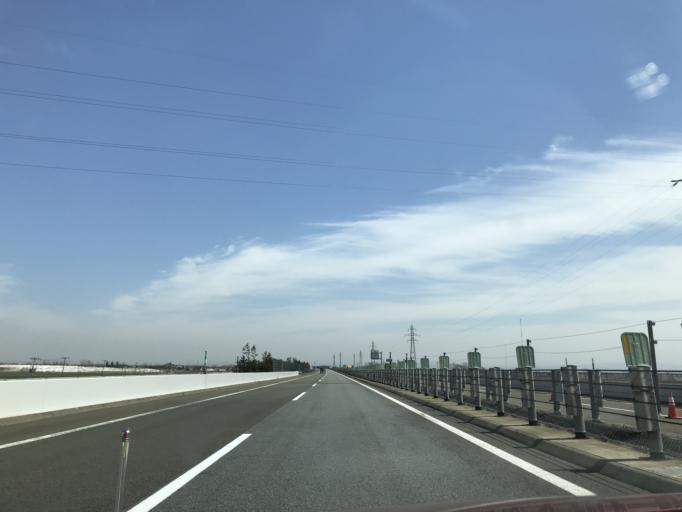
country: JP
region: Hokkaido
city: Ebetsu
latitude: 43.0846
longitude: 141.5589
